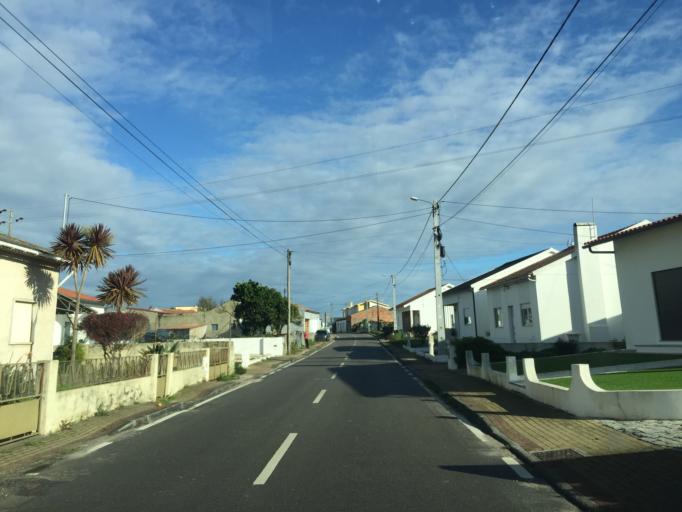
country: PT
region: Coimbra
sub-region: Figueira da Foz
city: Lavos
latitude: 40.0706
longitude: -8.8195
